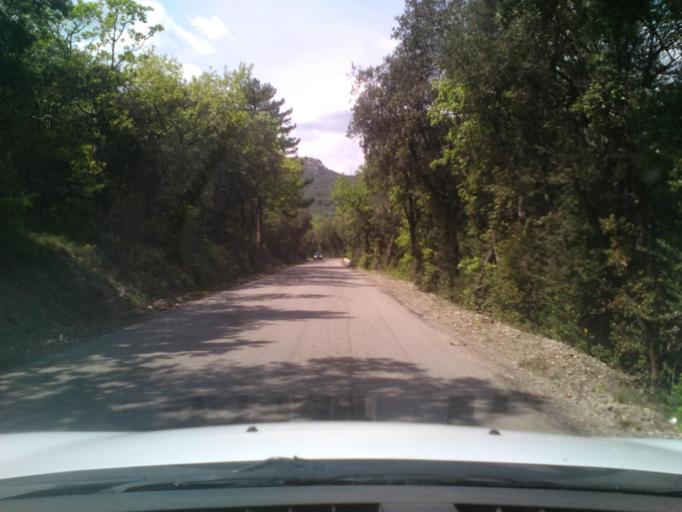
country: FR
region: Languedoc-Roussillon
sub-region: Departement du Gard
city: Saint-Hippolyte-du-Fort
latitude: 43.9792
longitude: 3.8883
